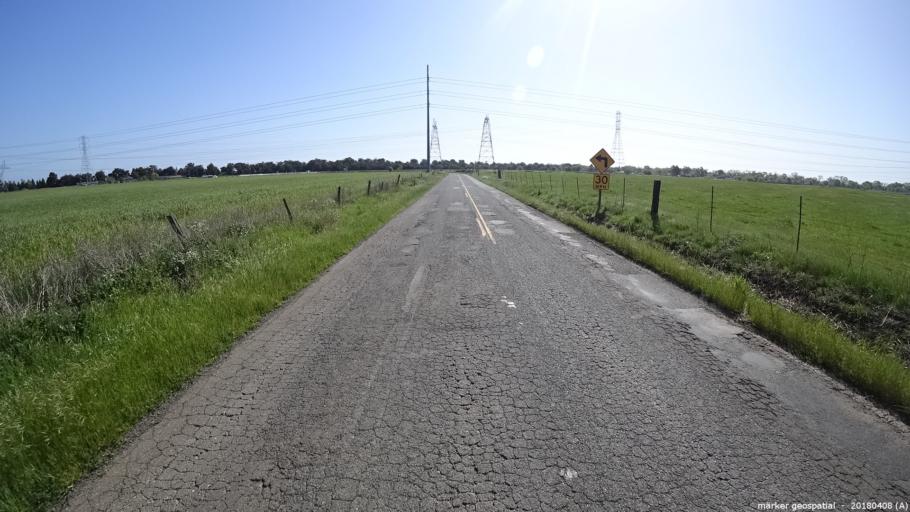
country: US
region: California
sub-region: Sacramento County
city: Elk Grove
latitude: 38.3618
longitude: -121.3547
